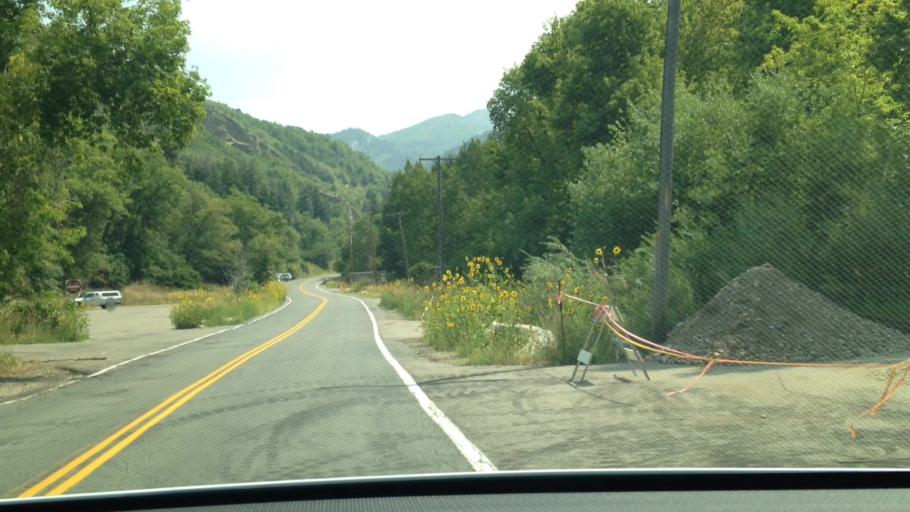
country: US
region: Utah
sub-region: Salt Lake County
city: Mount Olympus
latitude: 40.6995
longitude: -111.7191
